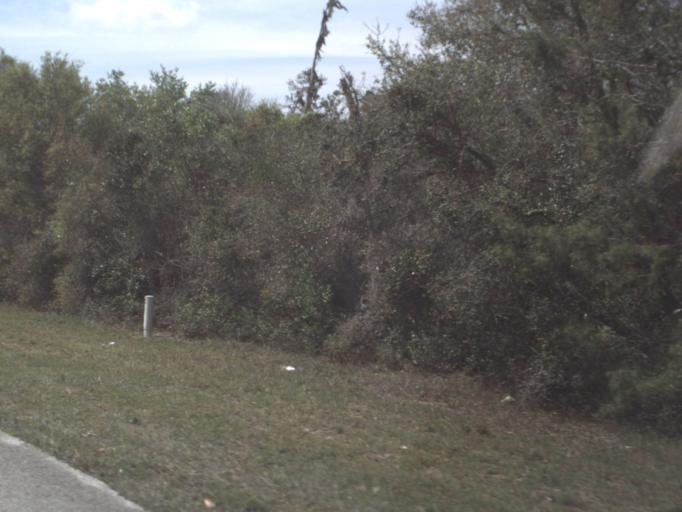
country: US
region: Florida
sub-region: Lake County
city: Astor
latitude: 29.2237
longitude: -81.6461
